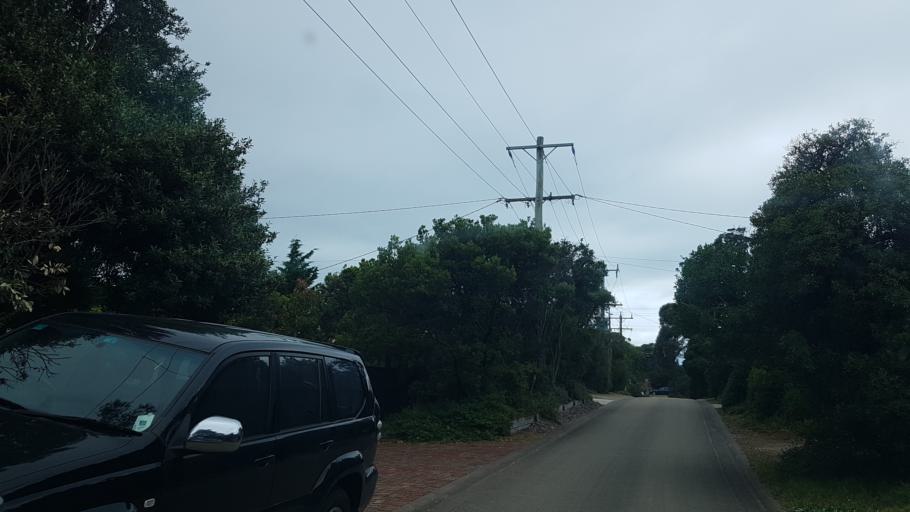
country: AU
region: Victoria
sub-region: Mornington Peninsula
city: Blairgowrie
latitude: -38.3771
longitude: 144.7792
